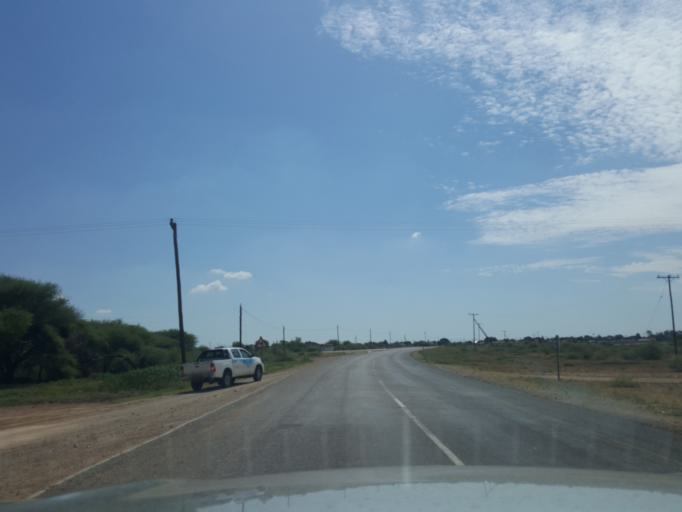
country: BW
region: Kweneng
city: Letlhakeng
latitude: -24.1167
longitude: 25.0419
